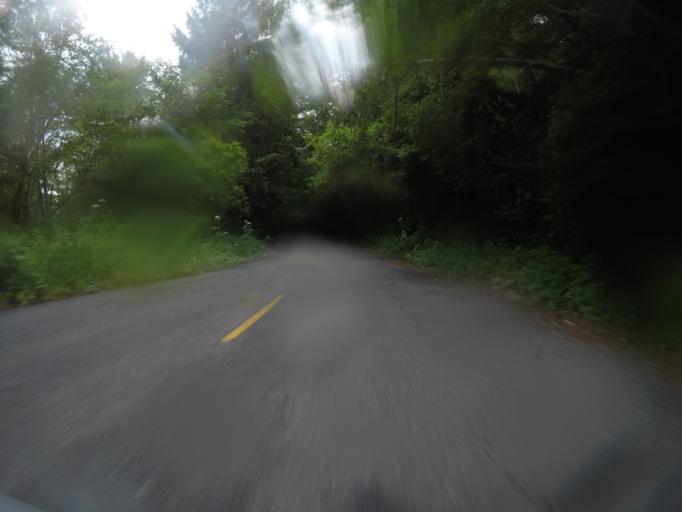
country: US
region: California
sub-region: Humboldt County
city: Westhaven-Moonstone
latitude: 41.3016
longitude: -124.0356
